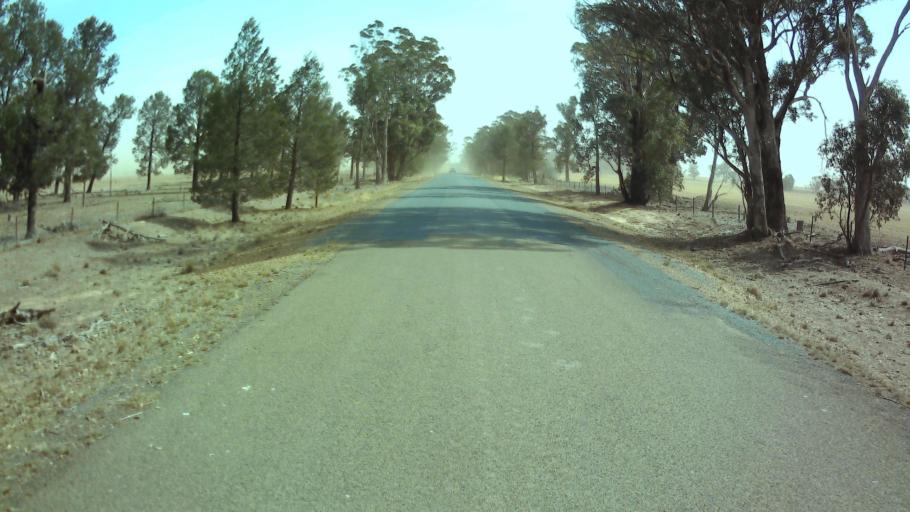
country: AU
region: New South Wales
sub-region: Weddin
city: Grenfell
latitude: -33.7549
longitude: 147.9900
